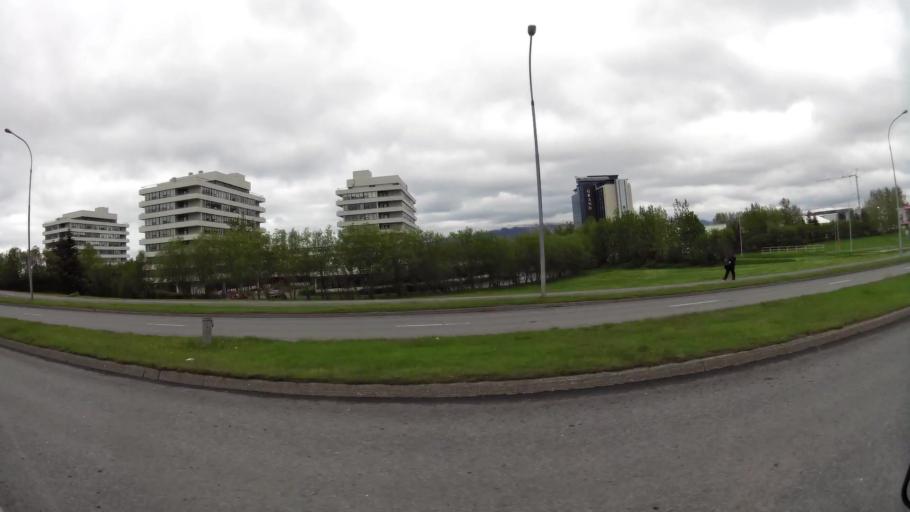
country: IS
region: Capital Region
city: Reykjavik
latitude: 64.1403
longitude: -21.8950
